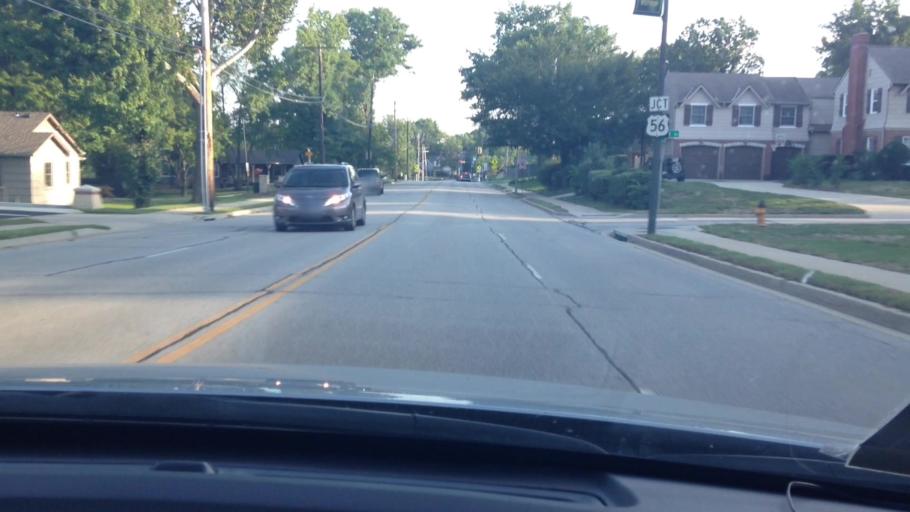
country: US
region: Kansas
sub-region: Johnson County
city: Westwood
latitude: 39.0364
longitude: -94.6119
